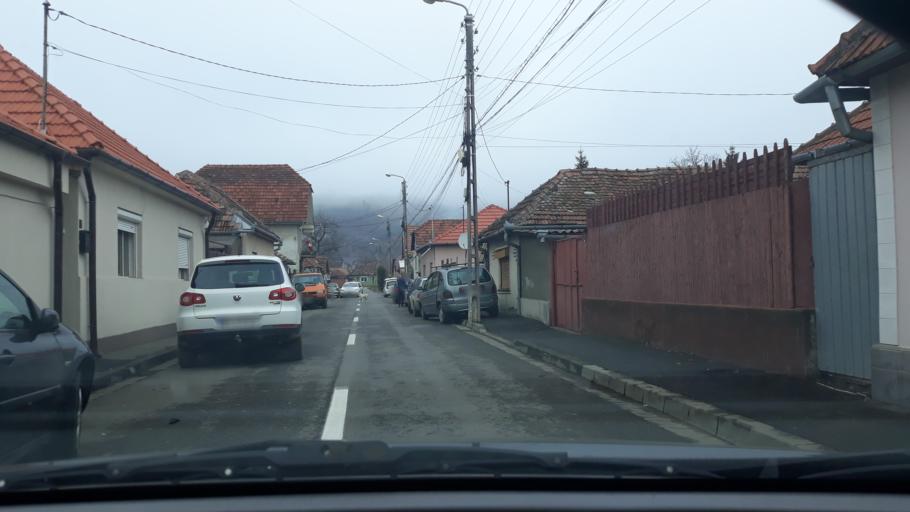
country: RO
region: Bihor
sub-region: Comuna Sanmartin
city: Sanmartin
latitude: 47.0481
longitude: 21.9726
